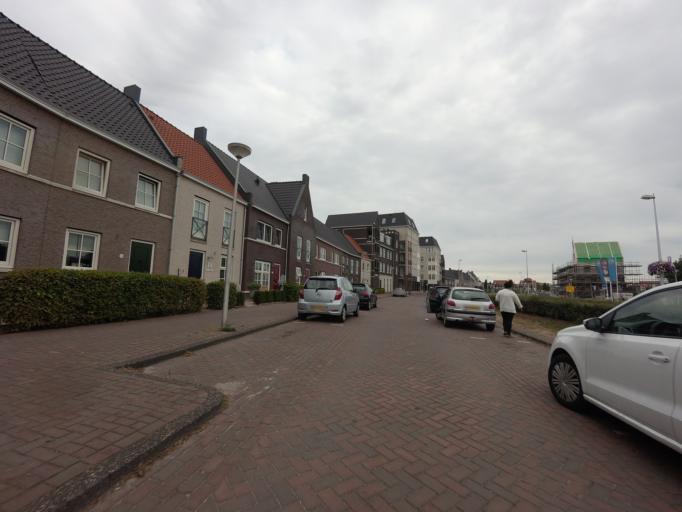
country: NL
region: Utrecht
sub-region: Stichtse Vecht
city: Spechtenkamp
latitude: 52.0929
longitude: 5.0147
